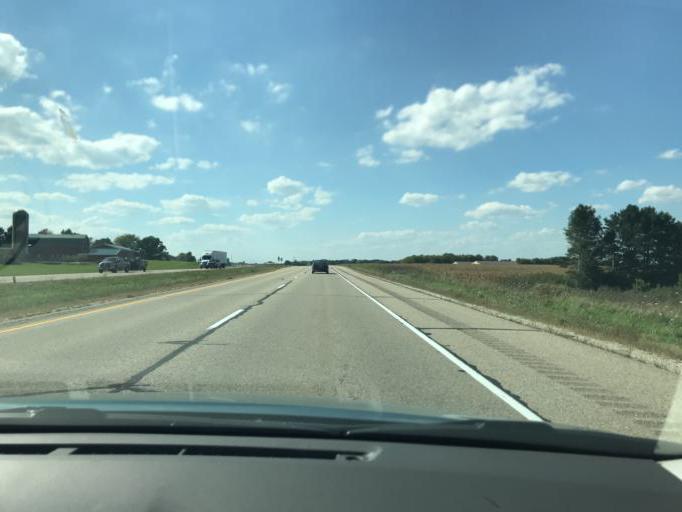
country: US
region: Wisconsin
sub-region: Kenosha County
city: Powers Lake
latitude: 42.5833
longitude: -88.2791
